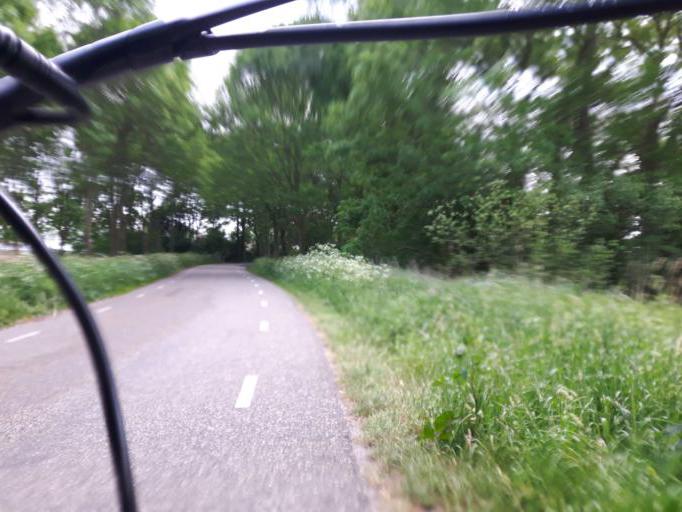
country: NL
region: North Brabant
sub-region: Gemeente Steenbergen
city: Welberg
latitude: 51.5553
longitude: 4.3533
